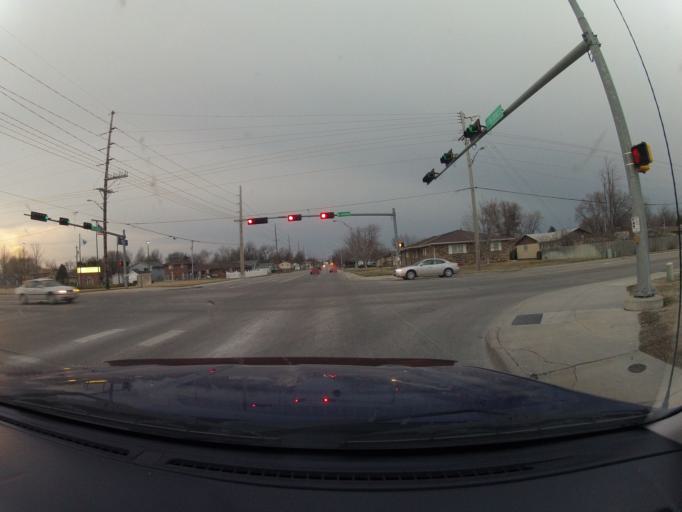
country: US
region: Nebraska
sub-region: Buffalo County
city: Kearney
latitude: 40.7139
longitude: -99.0646
